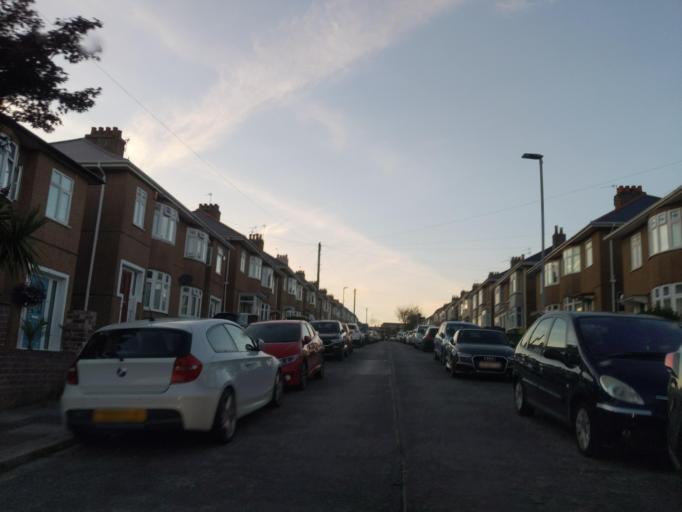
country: GB
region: England
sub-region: Plymouth
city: Plymouth
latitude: 50.3905
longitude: -4.1538
